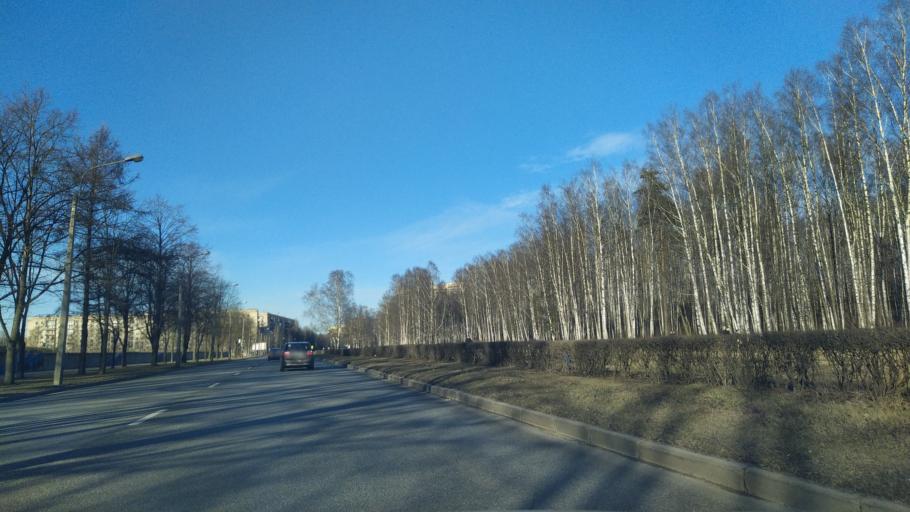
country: RU
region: Leningrad
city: Kalininskiy
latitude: 59.9965
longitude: 30.3924
